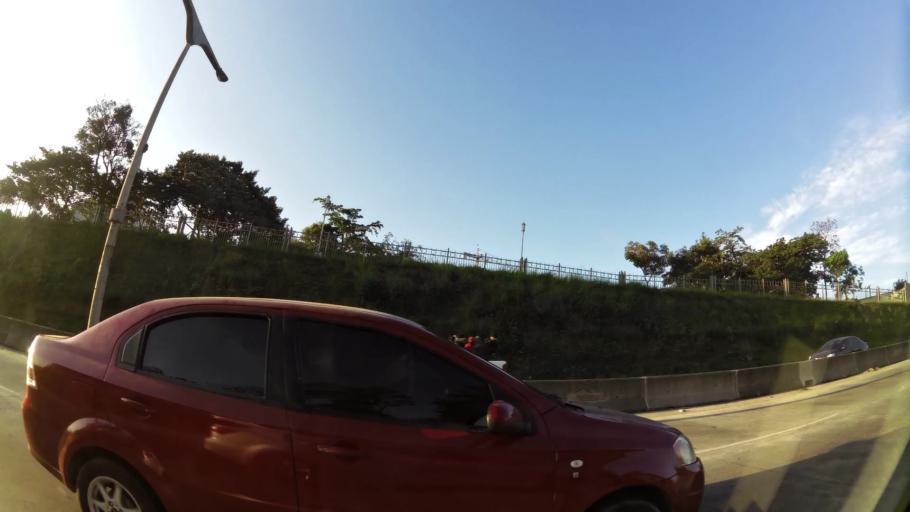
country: SV
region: La Libertad
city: Antiguo Cuscatlan
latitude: 13.6842
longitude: -89.2474
